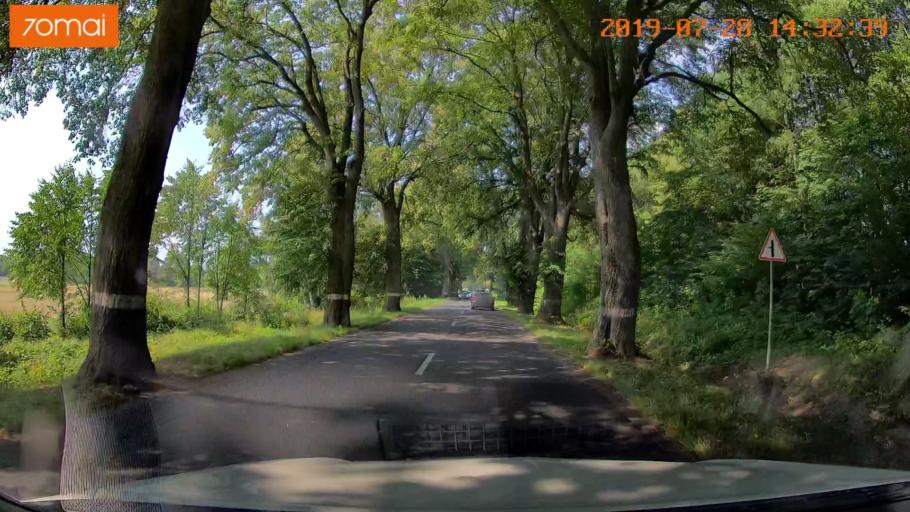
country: RU
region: Kaliningrad
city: Primorsk
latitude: 54.8141
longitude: 20.0394
